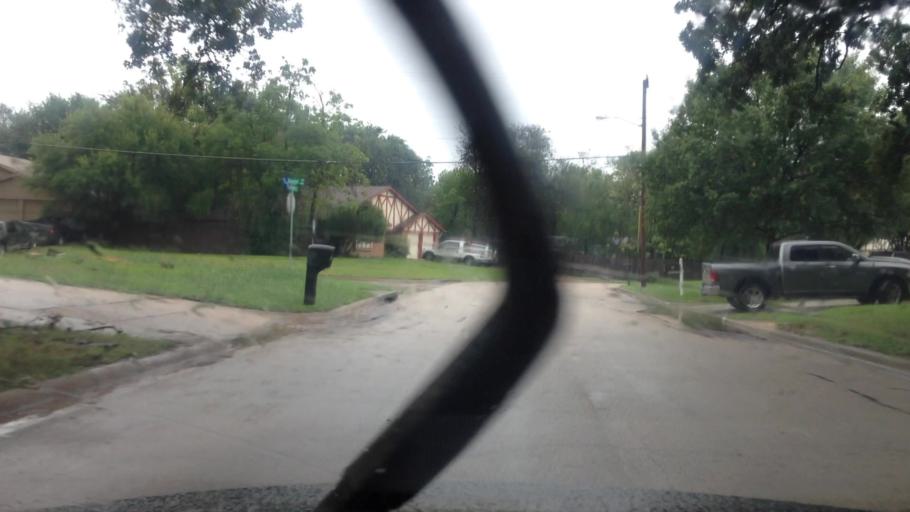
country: US
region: Texas
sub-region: Tarrant County
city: North Richland Hills
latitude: 32.8737
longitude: -97.2147
